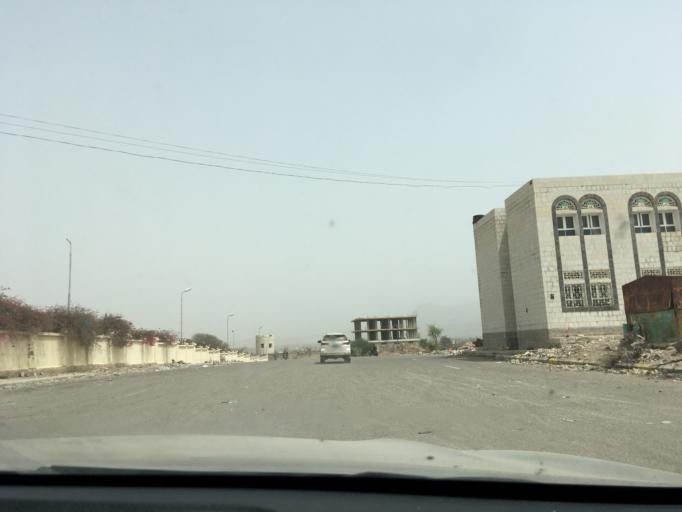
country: YE
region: Ad Dali'
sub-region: Qa'atabah
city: Qa`tabah
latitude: 13.8228
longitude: 44.7193
